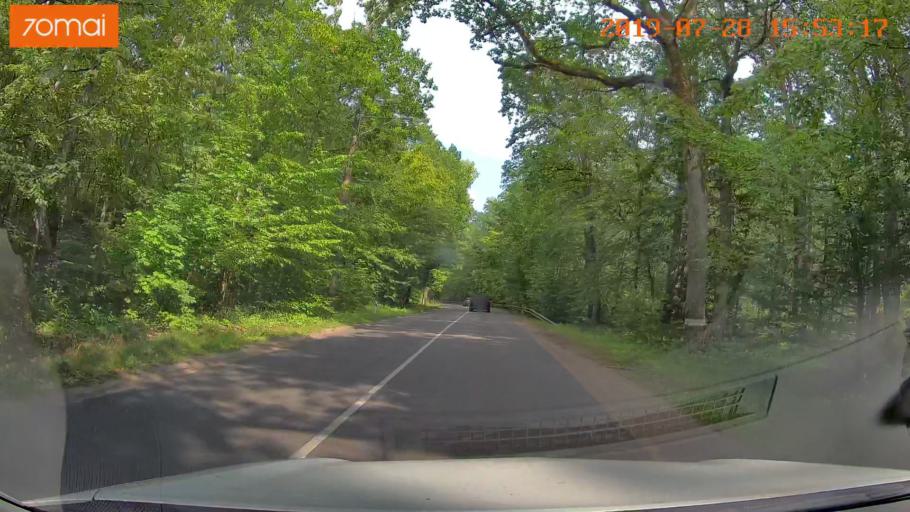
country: RU
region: Kaliningrad
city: Otradnoye
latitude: 54.9390
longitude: 20.1217
